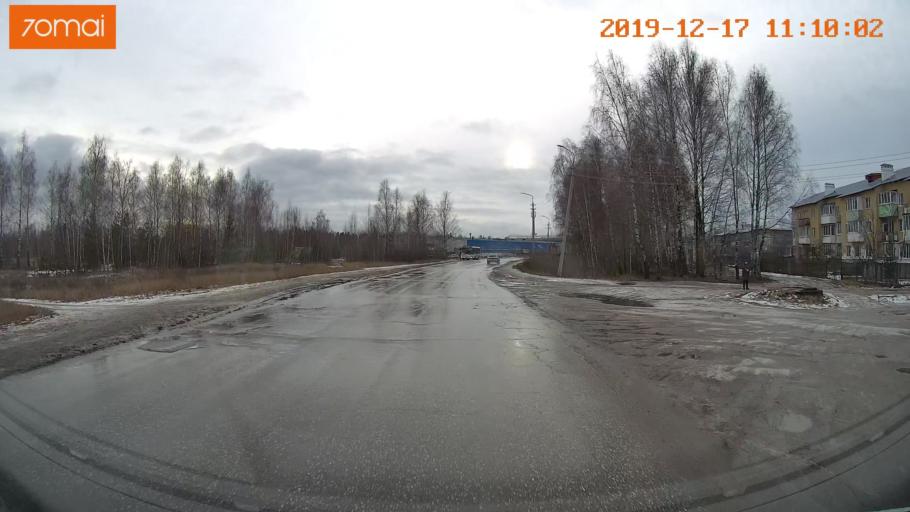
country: RU
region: Vladimir
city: Gus'-Khrustal'nyy
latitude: 55.5960
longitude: 40.6414
